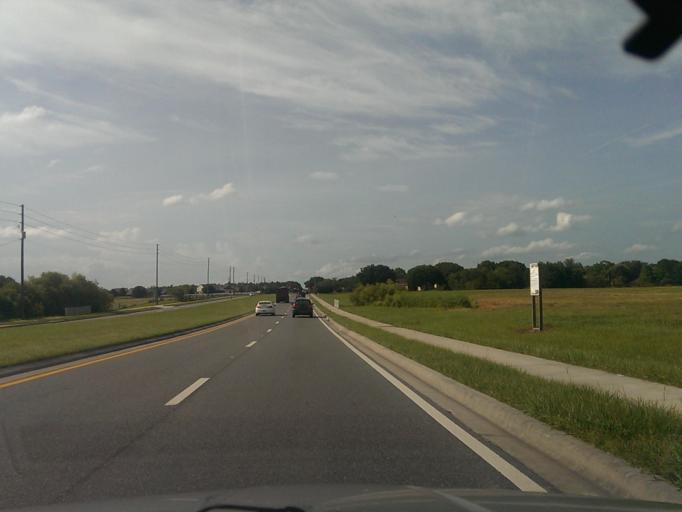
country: US
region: Florida
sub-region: Orange County
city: Lake Butler
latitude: 28.4832
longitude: -81.5827
